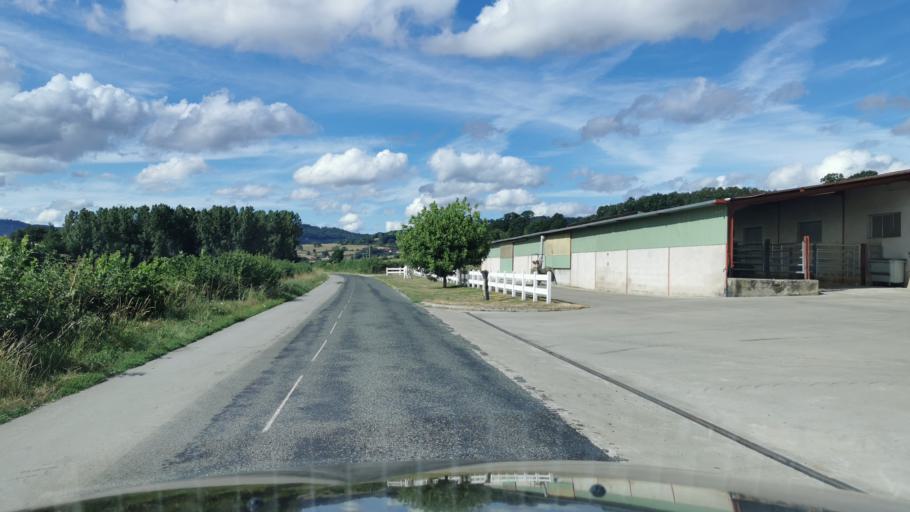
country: FR
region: Bourgogne
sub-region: Departement de Saone-et-Loire
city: Marmagne
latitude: 46.8401
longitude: 4.3190
